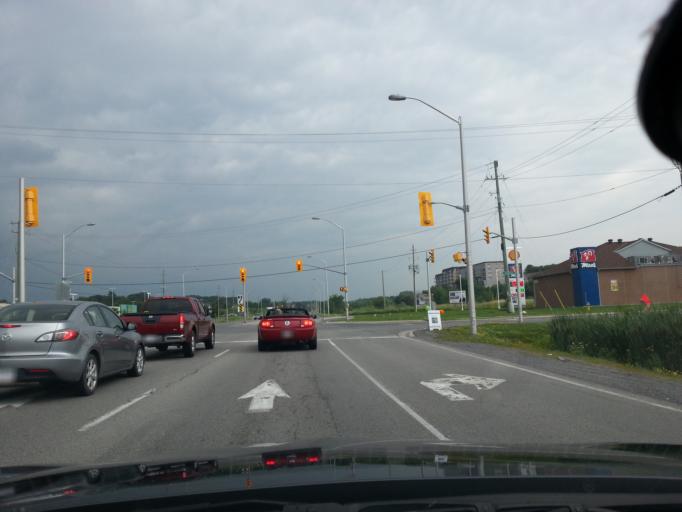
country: CA
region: Ontario
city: Clarence-Rockland
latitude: 45.5454
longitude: -75.3032
